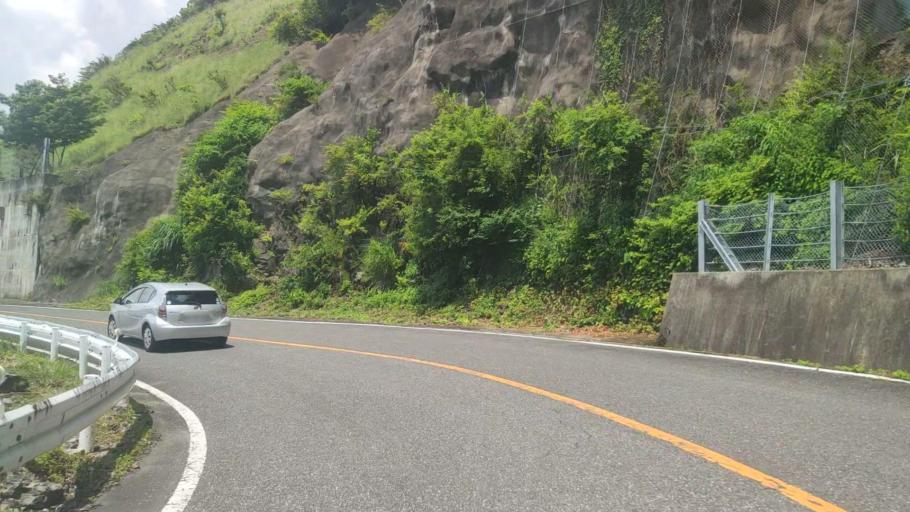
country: JP
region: Gifu
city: Tarui
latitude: 35.4016
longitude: 136.4265
